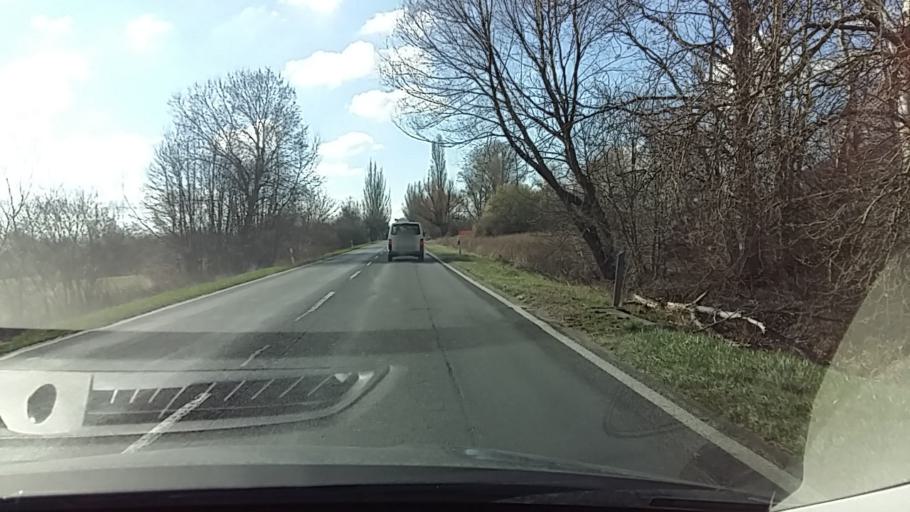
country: HU
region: Veszprem
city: Tapolca
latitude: 46.8223
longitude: 17.3806
